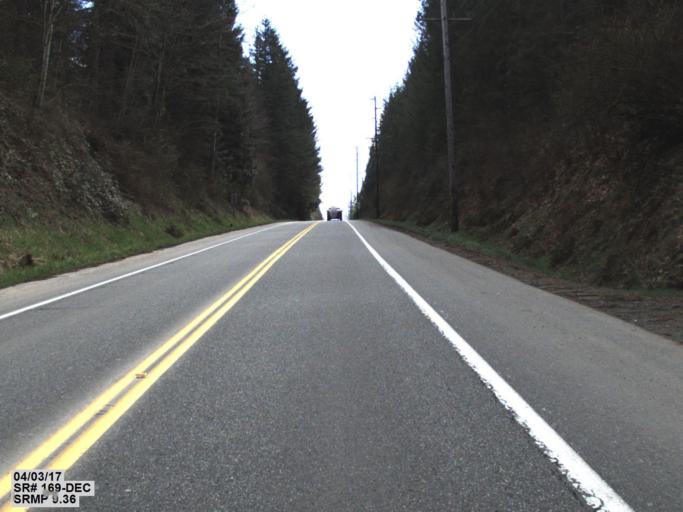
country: US
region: Washington
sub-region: King County
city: Black Diamond
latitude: 47.3327
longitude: -122.0114
